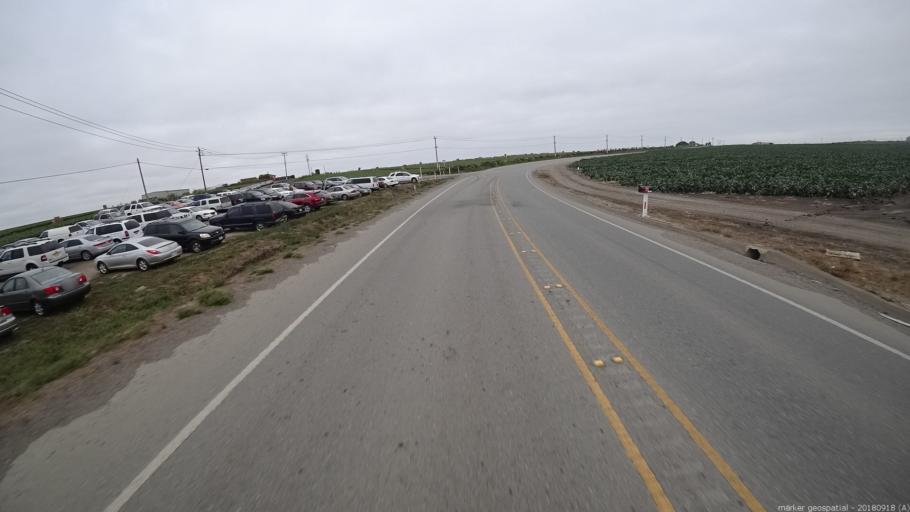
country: US
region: California
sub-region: Monterey County
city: Castroville
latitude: 36.7425
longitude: -121.7325
